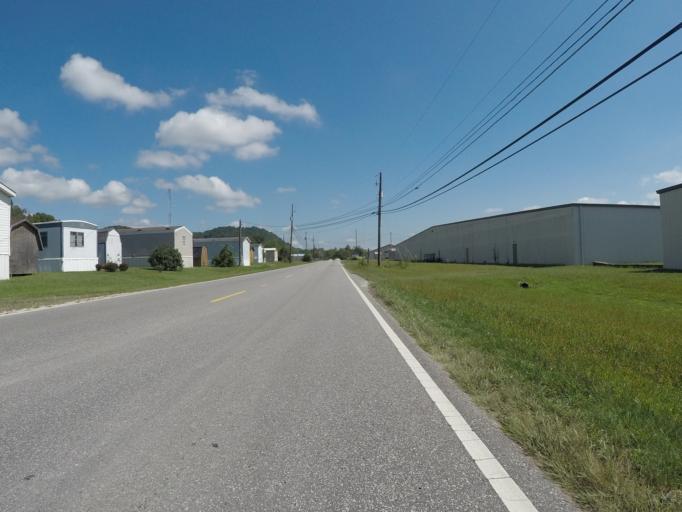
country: US
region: Ohio
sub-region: Lawrence County
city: Burlington
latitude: 38.4206
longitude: -82.4957
